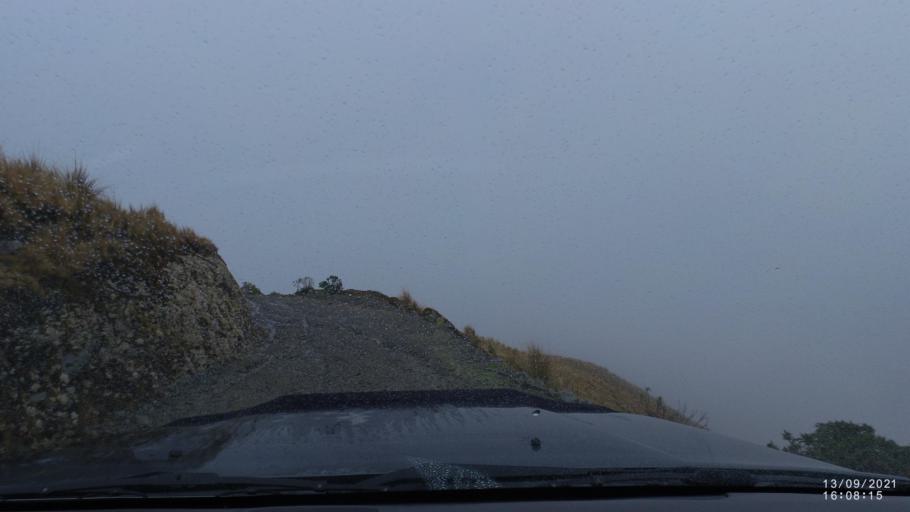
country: BO
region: Cochabamba
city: Colomi
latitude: -17.2781
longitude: -65.7085
